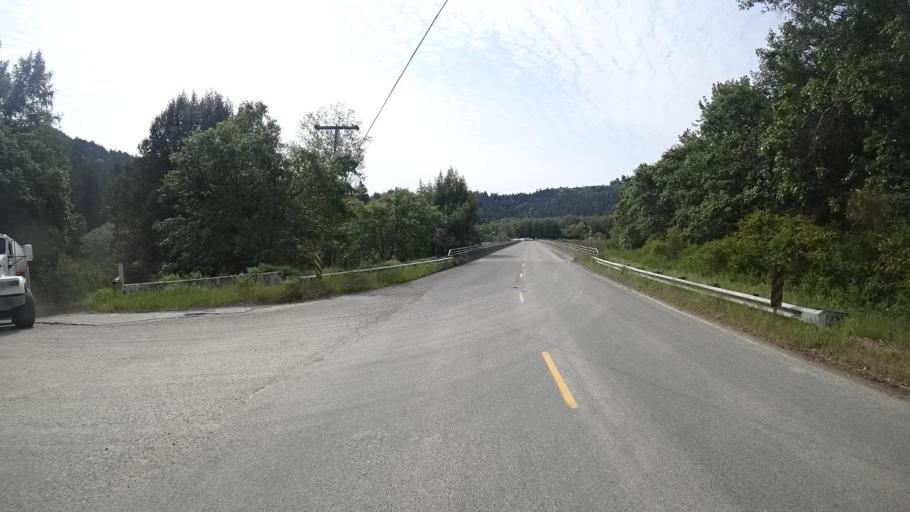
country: US
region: California
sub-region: Humboldt County
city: Redway
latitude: 40.0914
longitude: -123.7991
